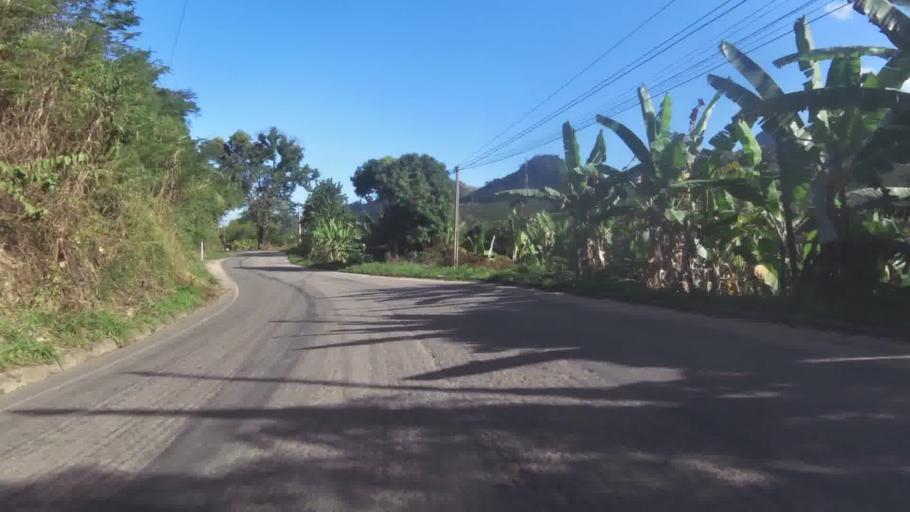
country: BR
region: Espirito Santo
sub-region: Iconha
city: Iconha
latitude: -20.7561
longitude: -40.8374
